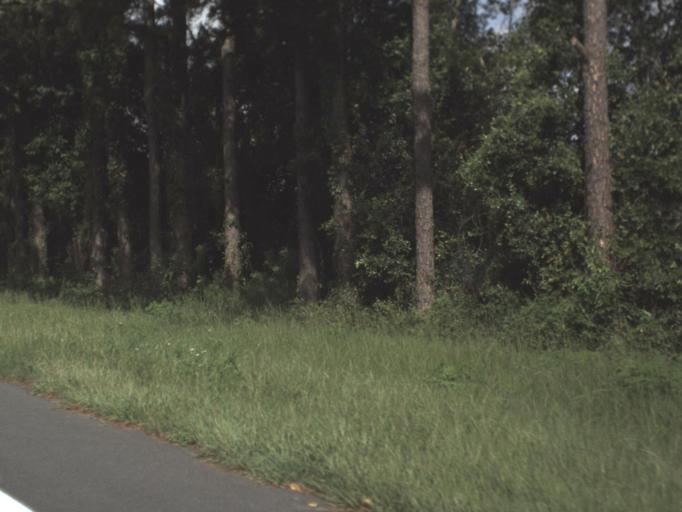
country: US
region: Florida
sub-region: Suwannee County
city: Wellborn
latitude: 30.0706
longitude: -82.7792
